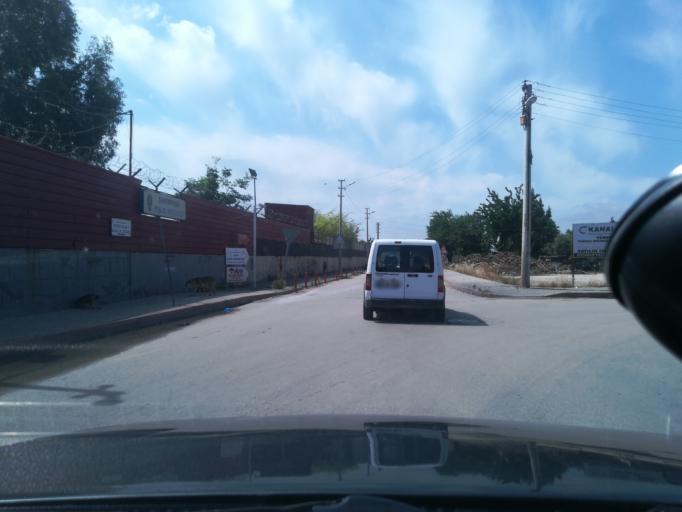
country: TR
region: Adana
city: Seyhan
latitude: 36.9882
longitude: 35.2864
